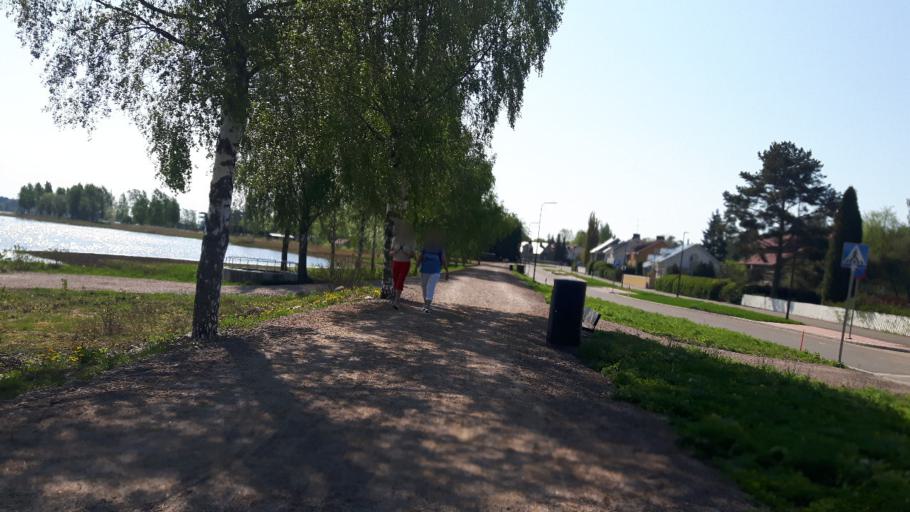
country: FI
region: Uusimaa
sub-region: Loviisa
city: Lovisa
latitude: 60.4499
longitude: 26.2348
